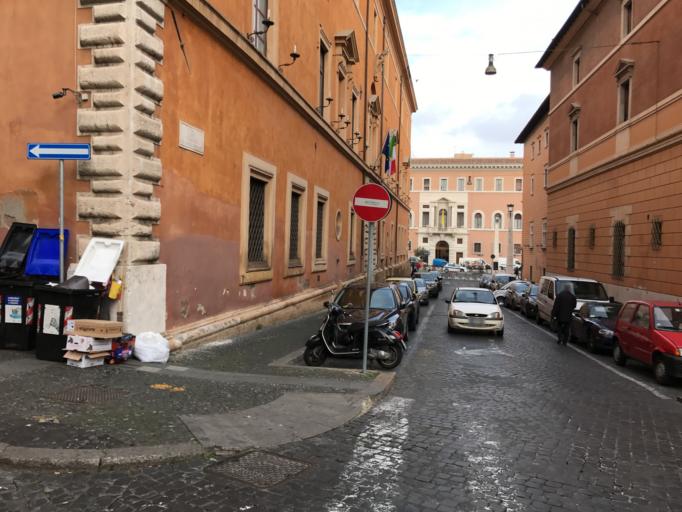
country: VA
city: Vatican City
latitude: 41.9015
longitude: 12.4606
